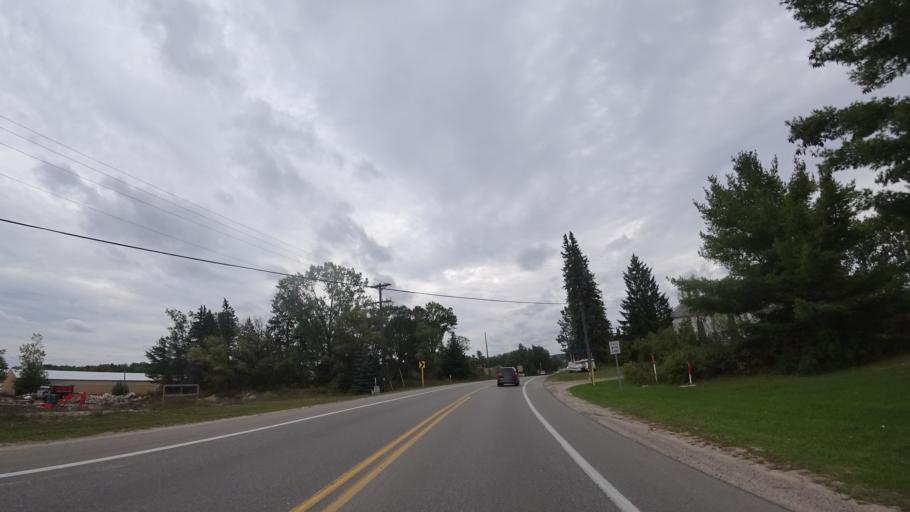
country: US
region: Michigan
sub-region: Emmet County
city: Petoskey
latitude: 45.4265
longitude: -84.9047
